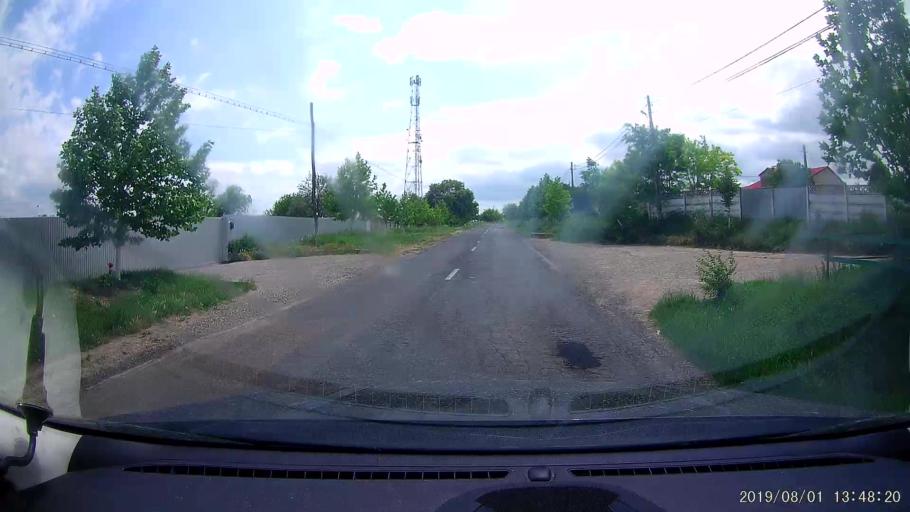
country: RO
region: Galati
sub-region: Comuna Oancea
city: Oancea
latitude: 45.9091
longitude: 28.1121
